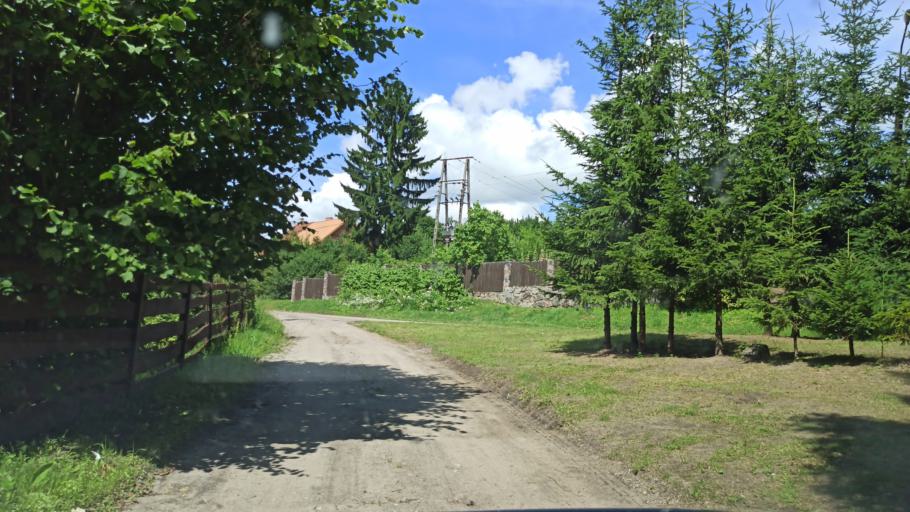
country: PL
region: Warmian-Masurian Voivodeship
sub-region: Powiat ostrodzki
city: Milakowo
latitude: 53.8595
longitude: 20.0653
